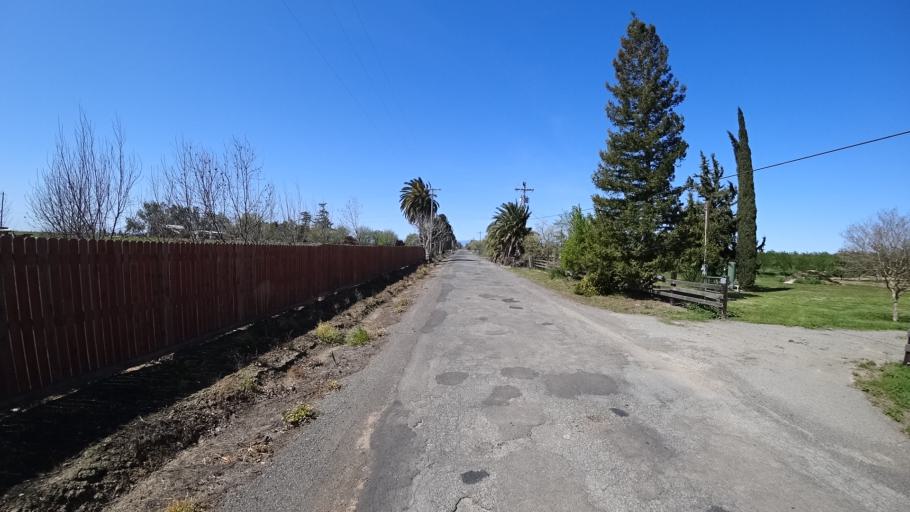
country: US
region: California
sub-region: Glenn County
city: Orland
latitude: 39.7969
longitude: -122.1083
